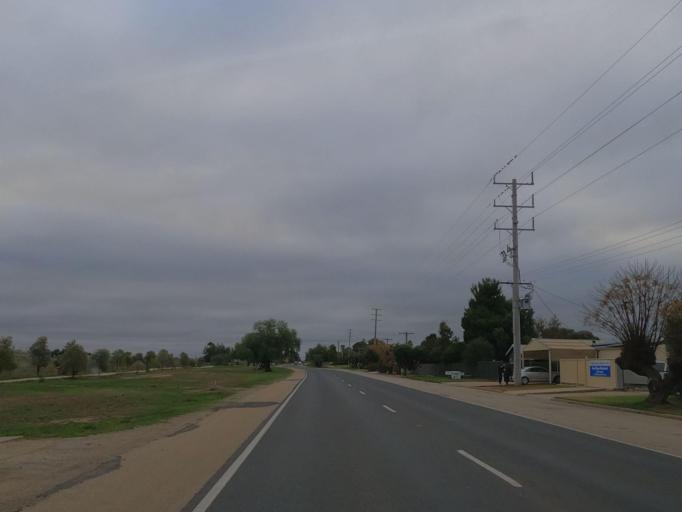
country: AU
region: Victoria
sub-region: Swan Hill
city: Swan Hill
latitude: -35.4592
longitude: 143.6321
